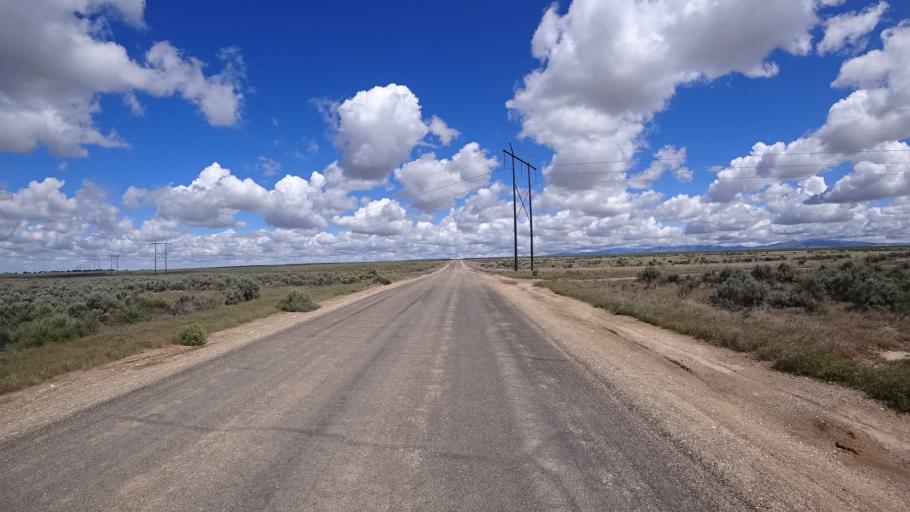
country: US
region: Idaho
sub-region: Ada County
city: Kuna
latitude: 43.4759
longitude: -116.2743
